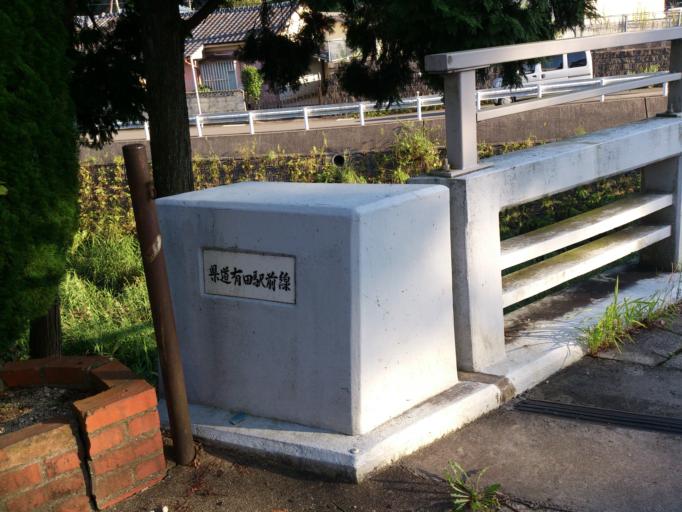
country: JP
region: Saga Prefecture
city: Imaricho-ko
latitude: 33.1815
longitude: 129.8809
